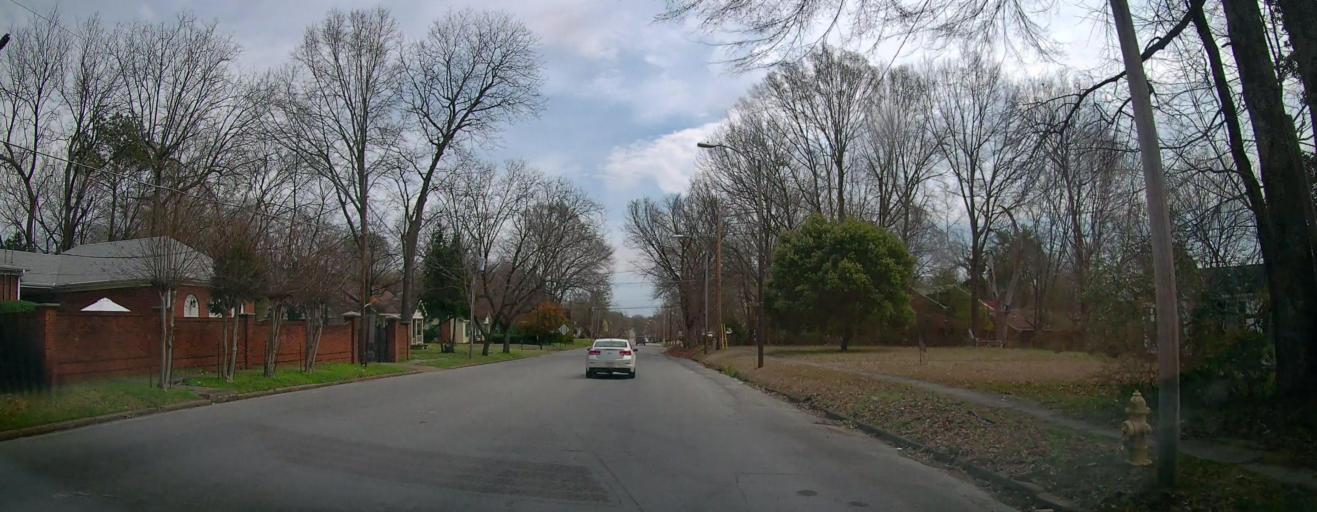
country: US
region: Mississippi
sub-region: Marshall County
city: Holly Springs
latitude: 34.7668
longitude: -89.4449
